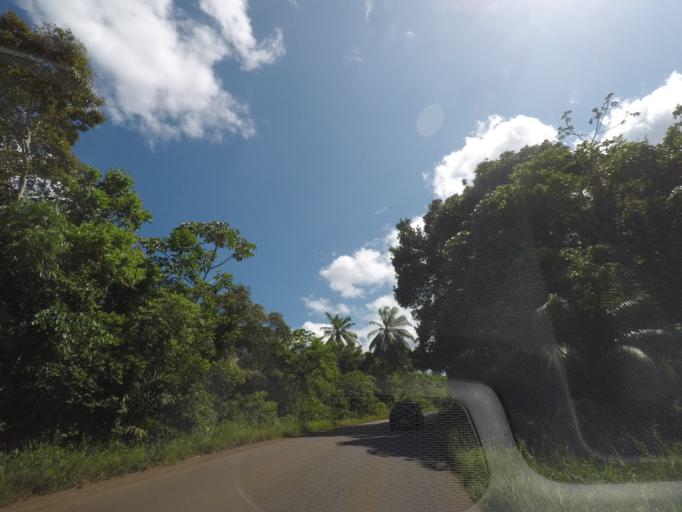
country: BR
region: Bahia
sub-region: Taperoa
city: Taperoa
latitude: -13.5868
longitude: -39.1053
